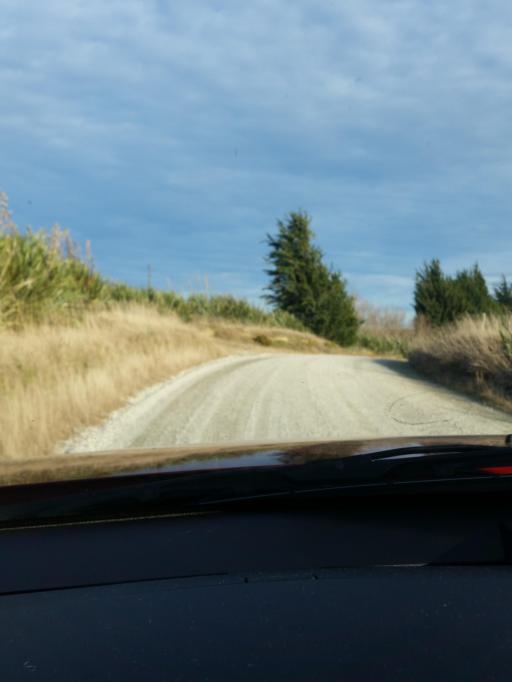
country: NZ
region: Southland
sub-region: Gore District
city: Gore
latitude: -46.2244
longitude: 168.7804
